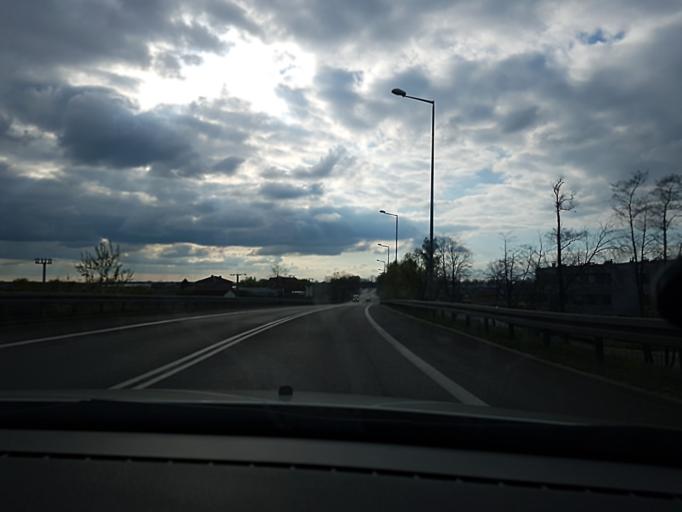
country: PL
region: Lodz Voivodeship
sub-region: powiat Lowicki
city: Lowicz
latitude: 52.1186
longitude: 19.9403
